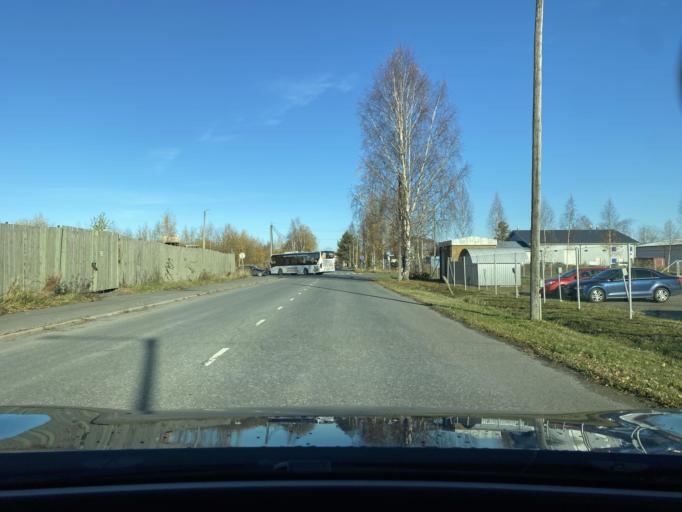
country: FI
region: Haeme
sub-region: Haemeenlinna
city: Parola
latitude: 61.0137
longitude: 24.4058
